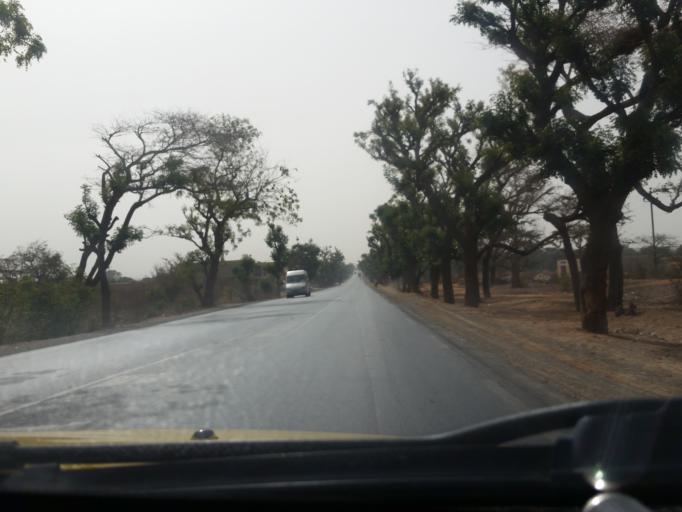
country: SN
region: Thies
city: Pout
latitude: 14.7653
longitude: -17.0804
